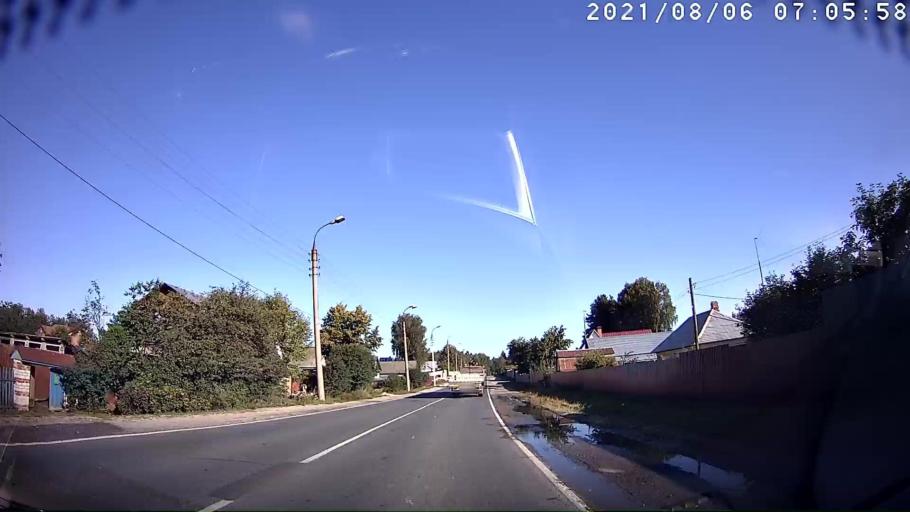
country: RU
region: Mariy-El
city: Yoshkar-Ola
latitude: 56.5562
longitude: 47.9835
